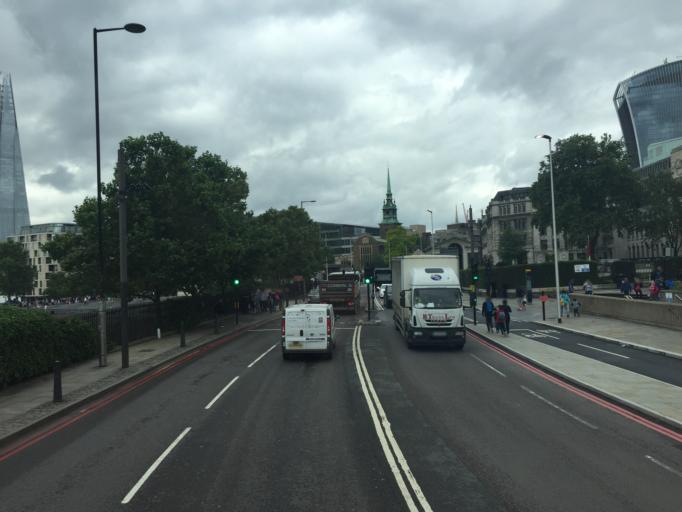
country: GB
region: England
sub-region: Greater London
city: City of London
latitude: 51.5096
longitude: -0.0761
